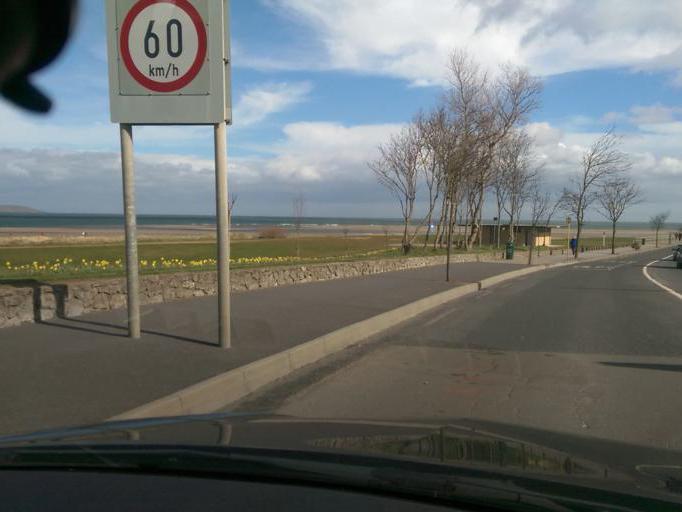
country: IE
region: Leinster
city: Malahide
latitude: 53.4489
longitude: -6.1381
